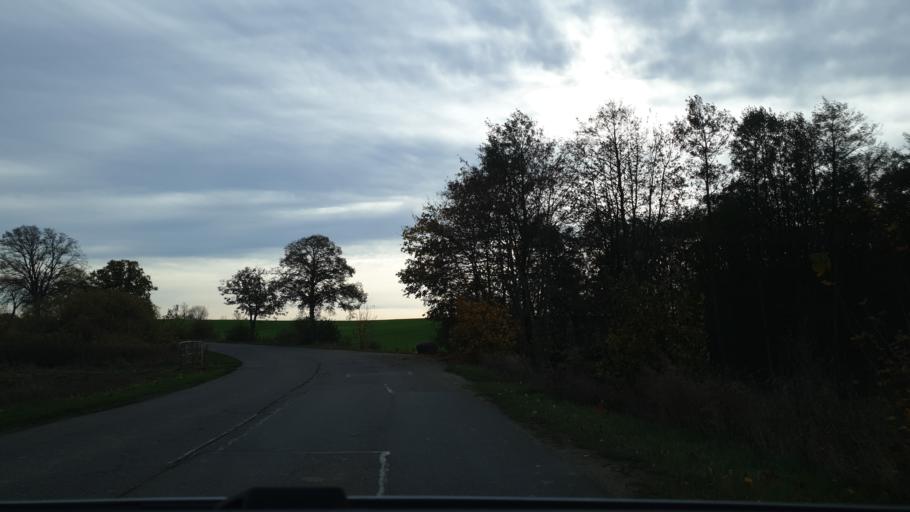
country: PL
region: Pomeranian Voivodeship
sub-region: Powiat pucki
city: Gniezdzewo
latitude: 54.7166
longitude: 18.3320
